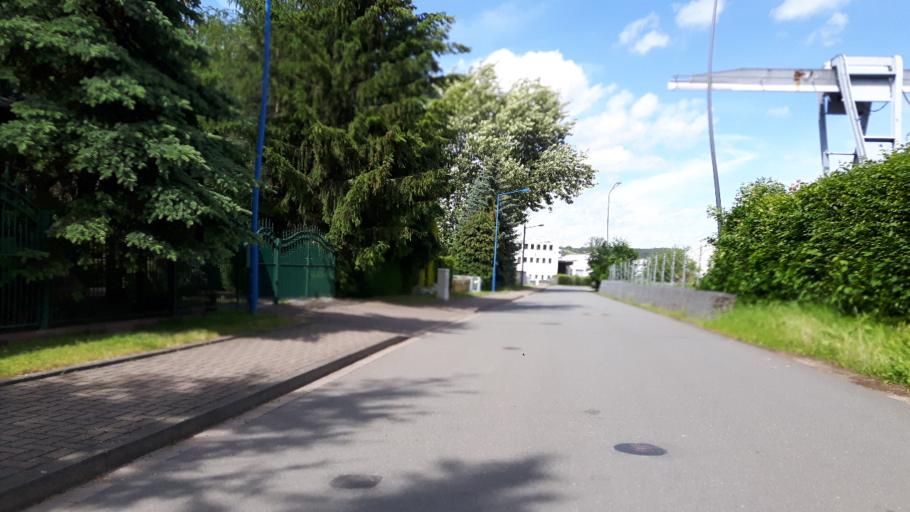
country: DE
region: Thuringia
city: Stadtilm
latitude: 50.7775
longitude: 11.0911
